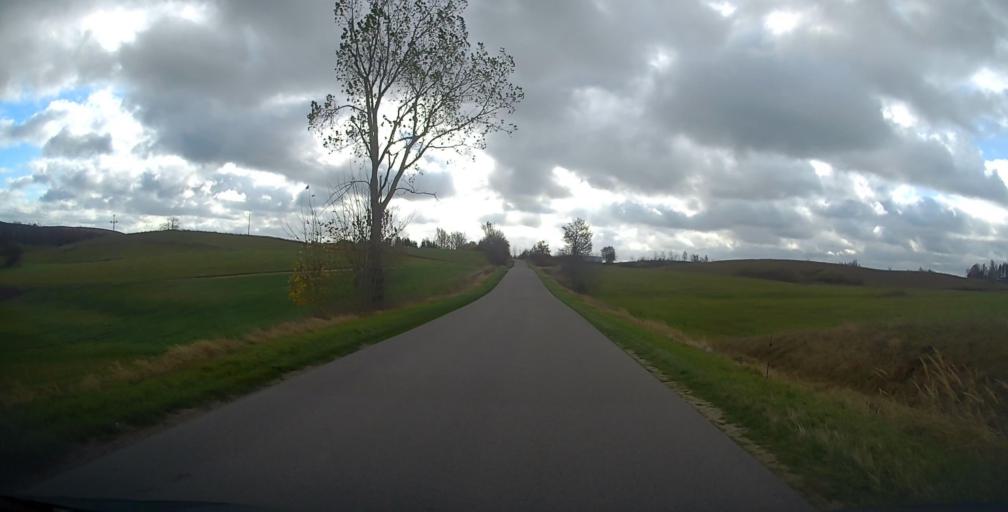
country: PL
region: Podlasie
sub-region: Suwalki
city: Suwalki
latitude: 54.3586
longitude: 22.8550
